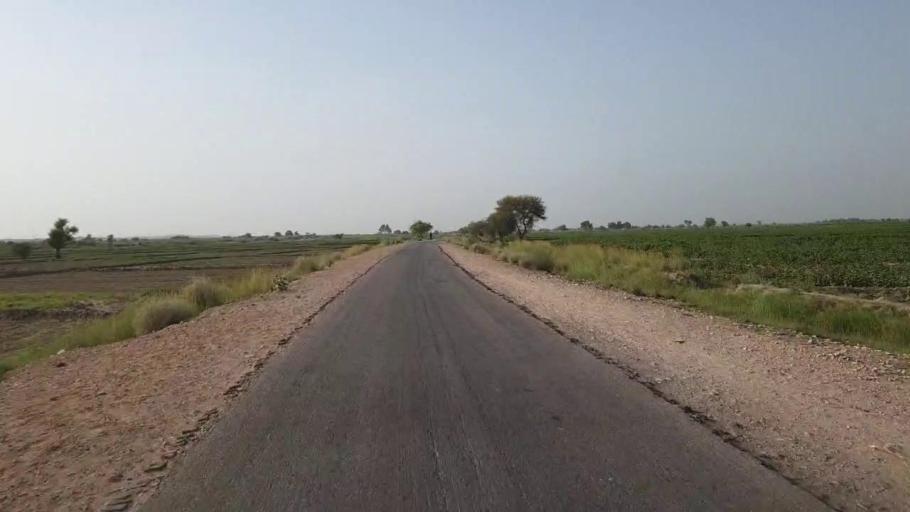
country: PK
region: Sindh
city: Jam Sahib
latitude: 26.4605
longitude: 68.8588
